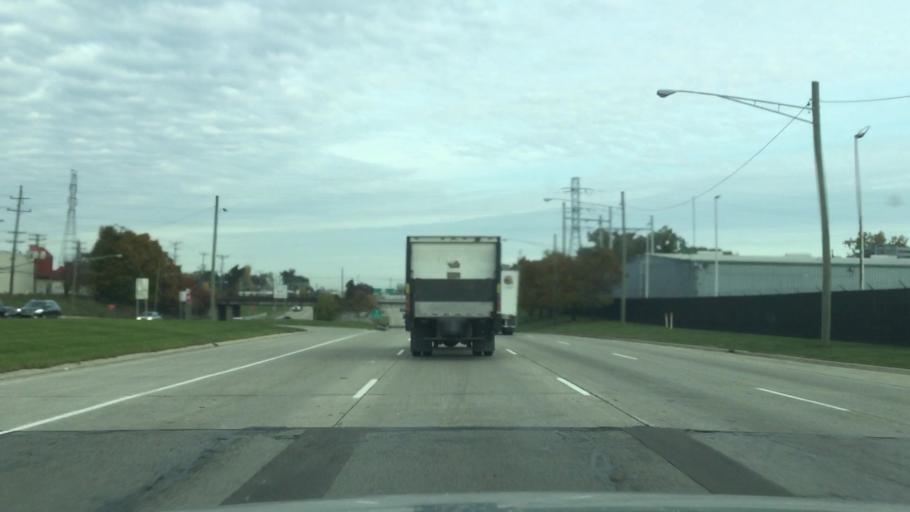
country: US
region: Michigan
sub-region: Wayne County
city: Redford
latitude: 42.3765
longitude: -83.2753
